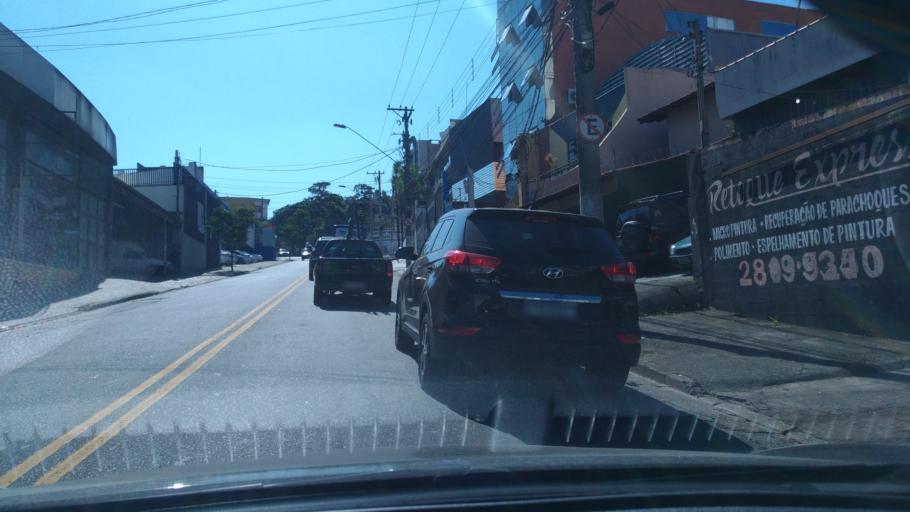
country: BR
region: Sao Paulo
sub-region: Santo Andre
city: Santo Andre
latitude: -23.6685
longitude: -46.5506
